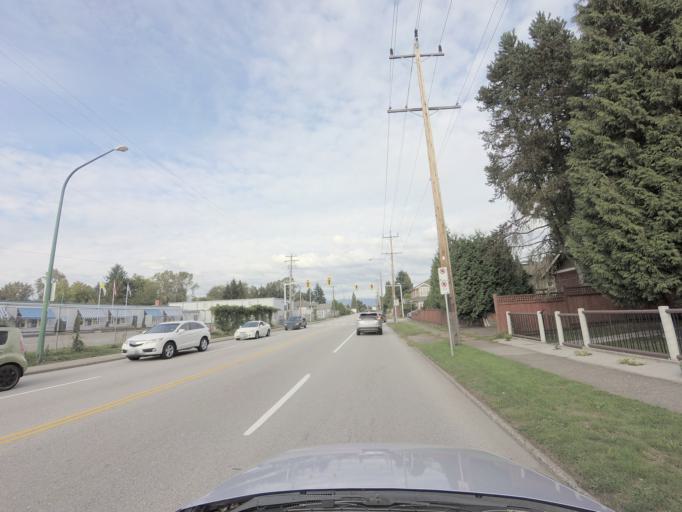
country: CA
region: British Columbia
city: New Westminster
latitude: 49.2146
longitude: -122.9357
